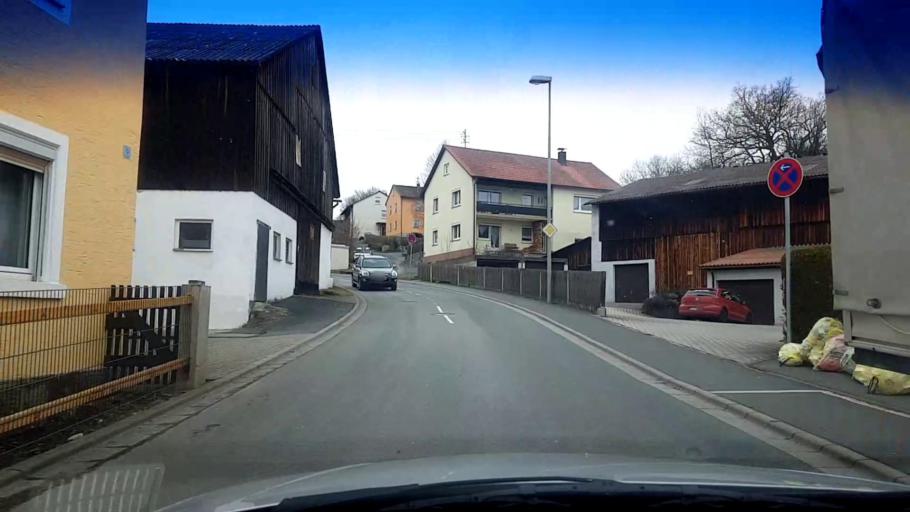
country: DE
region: Bavaria
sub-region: Upper Franconia
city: Untersteinach
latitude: 50.1323
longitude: 11.5254
